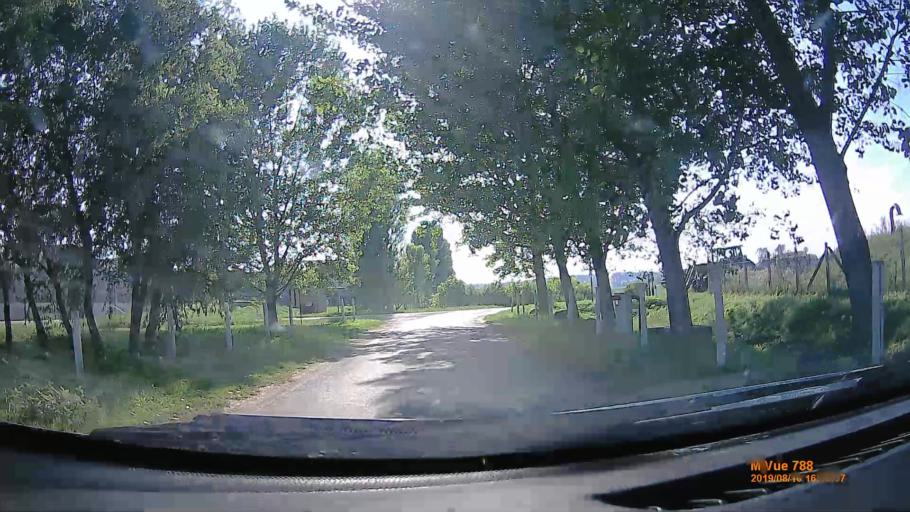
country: HU
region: Somogy
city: Balatonfenyves
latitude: 46.6820
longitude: 17.4992
